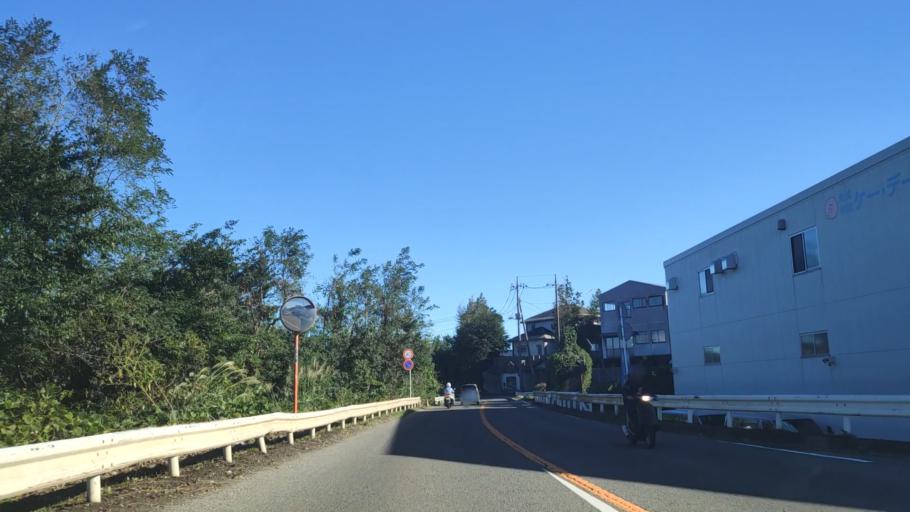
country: JP
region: Kanagawa
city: Zama
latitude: 35.5197
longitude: 139.3618
